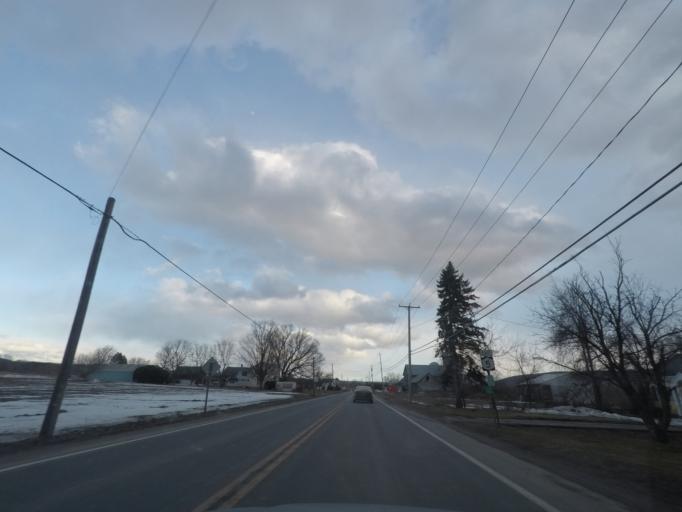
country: US
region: New York
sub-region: Oneida County
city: Utica
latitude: 43.0980
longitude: -75.1504
